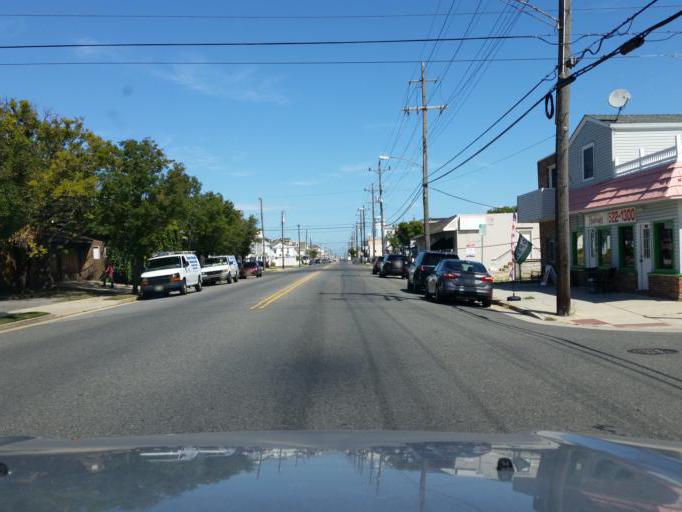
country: US
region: New Jersey
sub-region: Cape May County
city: North Wildwood
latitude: 39.0012
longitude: -74.8017
